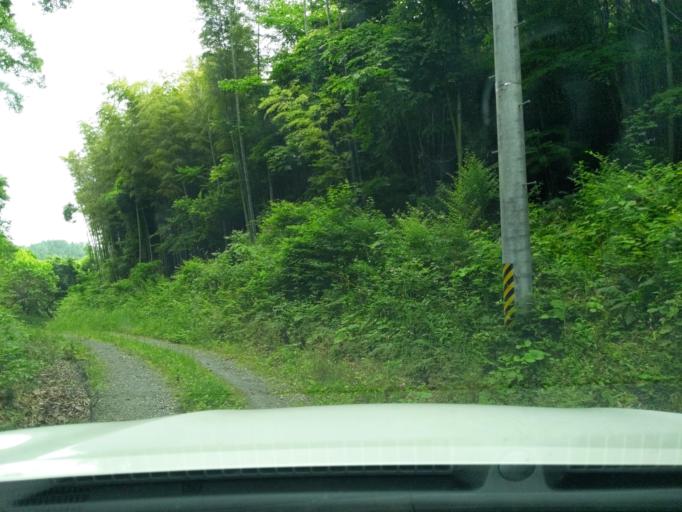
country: JP
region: Fukushima
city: Koriyama
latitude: 37.4038
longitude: 140.4354
